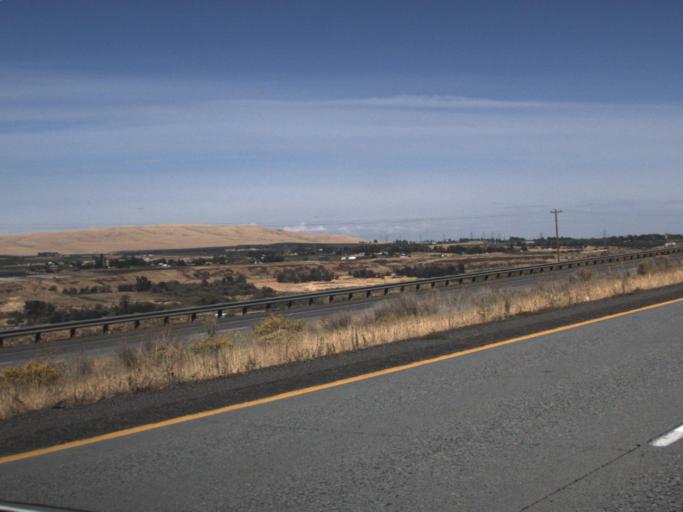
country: US
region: Washington
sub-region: Benton County
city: Benton City
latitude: 46.2665
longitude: -119.5635
